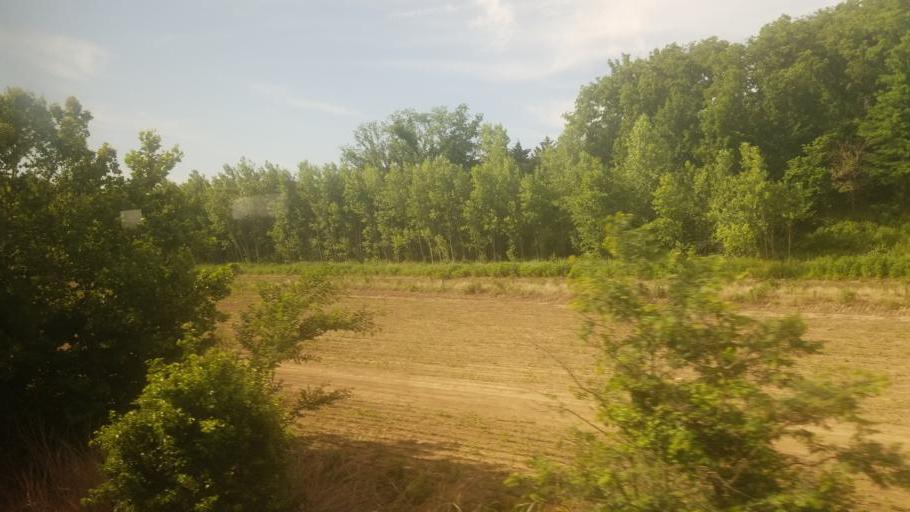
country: US
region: Kansas
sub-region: Wyandotte County
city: Edwardsville
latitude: 39.0485
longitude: -94.8334
